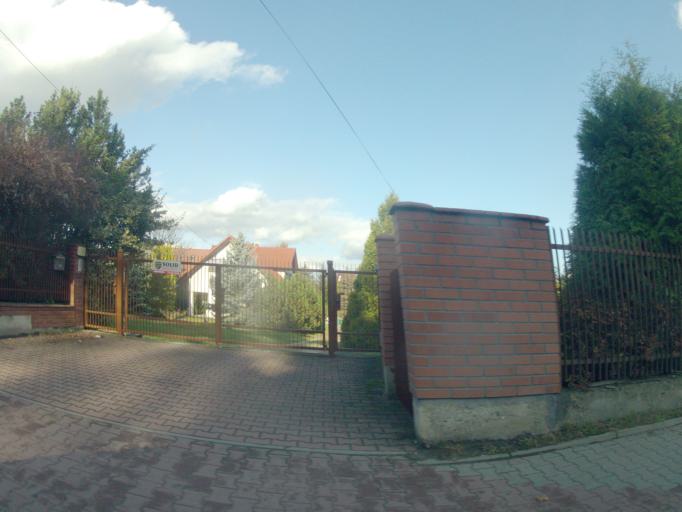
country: PL
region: Lesser Poland Voivodeship
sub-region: Powiat krakowski
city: Rzaska
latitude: 50.0678
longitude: 19.8674
